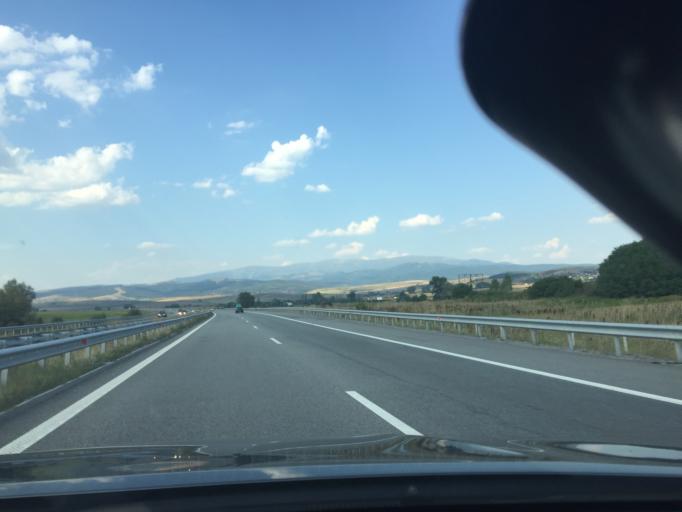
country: BG
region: Kyustendil
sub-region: Obshtina Bobovdol
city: Bobovdol
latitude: 42.3883
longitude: 23.1170
